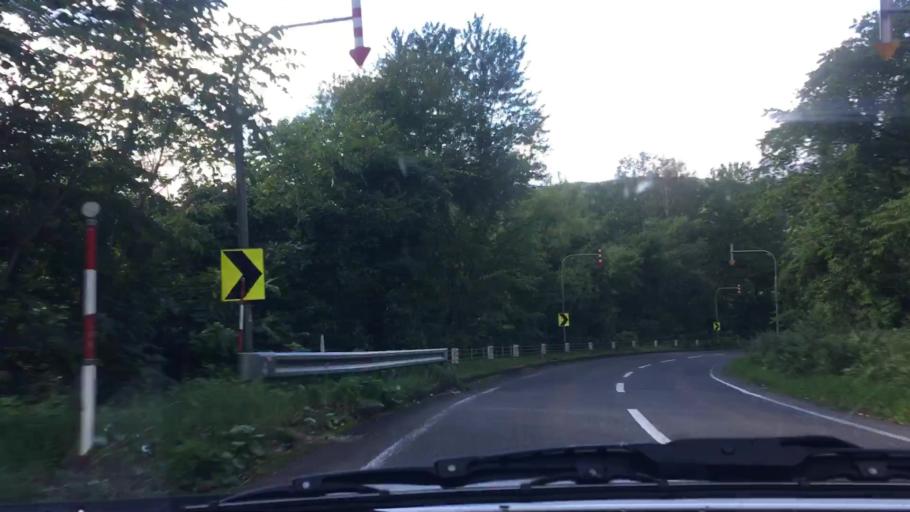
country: JP
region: Hokkaido
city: Otofuke
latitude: 43.1782
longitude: 142.9297
